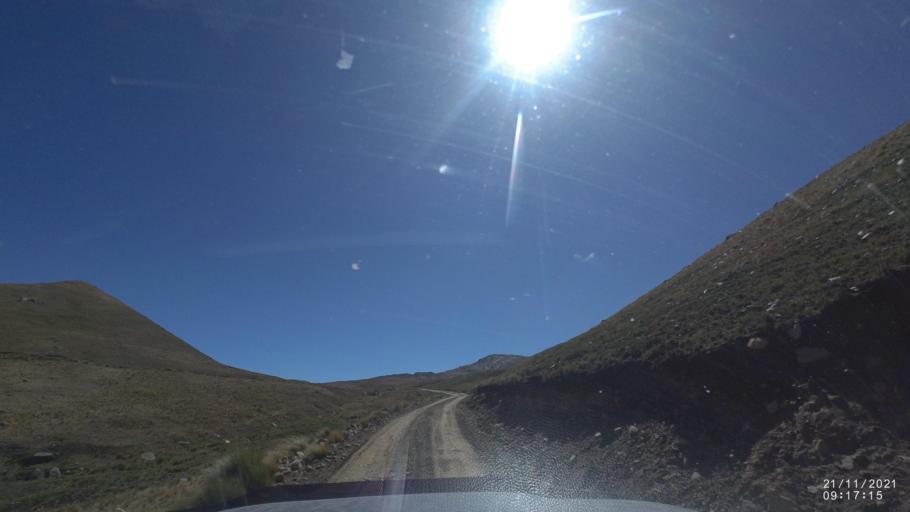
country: BO
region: Cochabamba
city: Cochabamba
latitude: -17.1228
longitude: -66.2576
